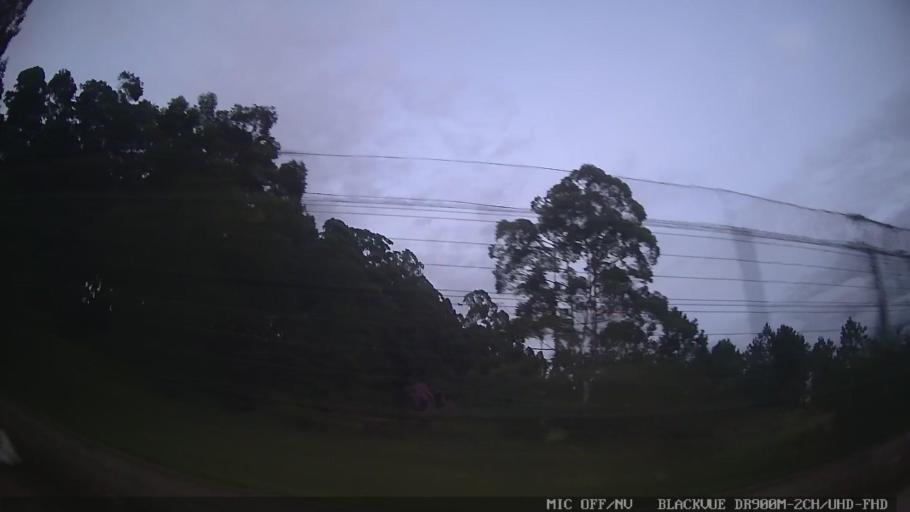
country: BR
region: Sao Paulo
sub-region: Itaquaquecetuba
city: Itaquaquecetuba
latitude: -23.4663
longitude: -46.3549
